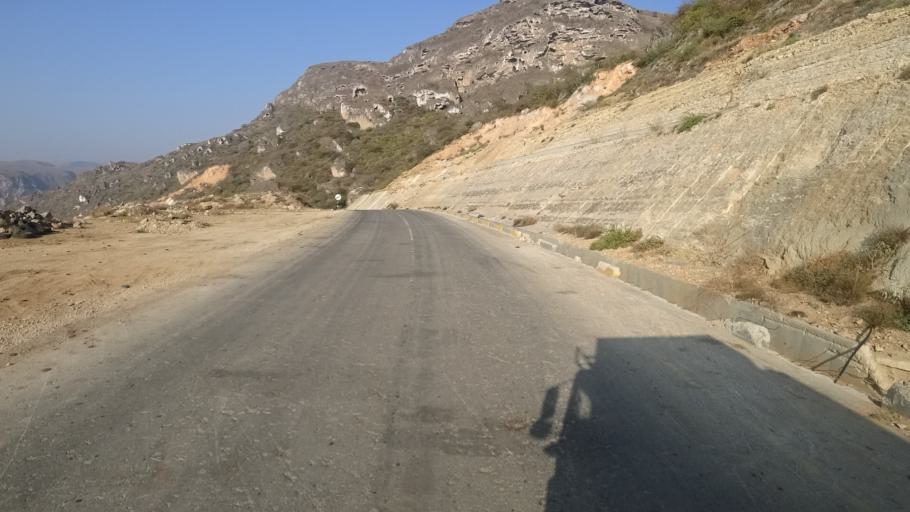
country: YE
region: Al Mahrah
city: Hawf
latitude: 16.7573
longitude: 53.2255
